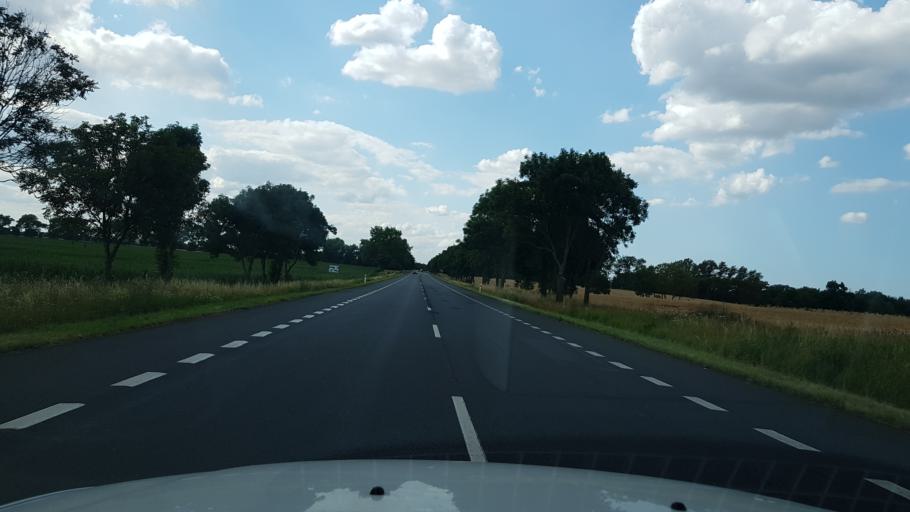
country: PL
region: West Pomeranian Voivodeship
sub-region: Powiat pyrzycki
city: Pyrzyce
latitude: 53.1935
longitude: 14.8318
